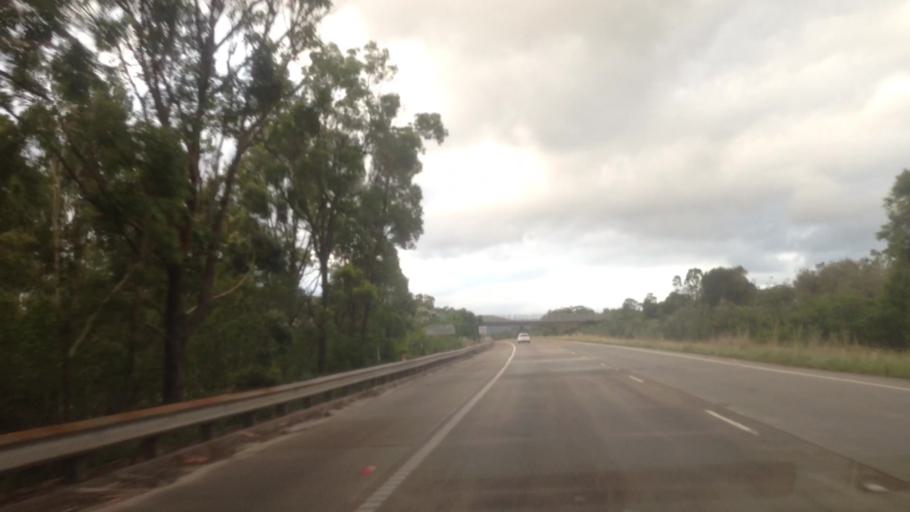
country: AU
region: New South Wales
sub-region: Wyong Shire
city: Charmhaven
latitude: -33.1851
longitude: 151.4674
